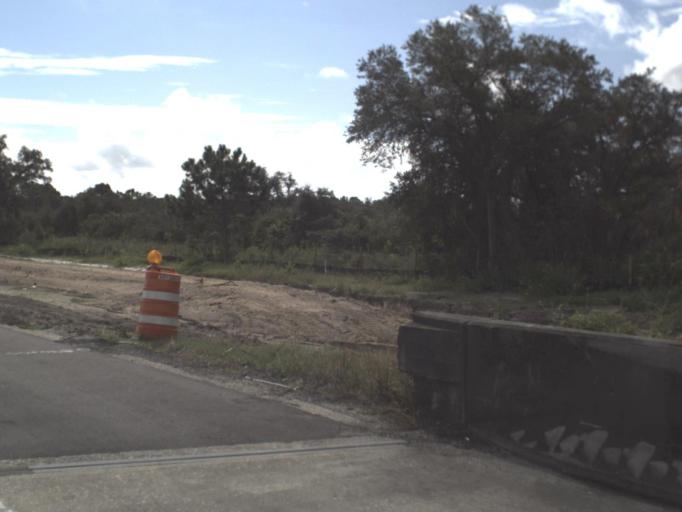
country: US
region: Florida
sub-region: Sarasota County
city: Warm Mineral Springs
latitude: 27.0998
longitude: -82.2713
